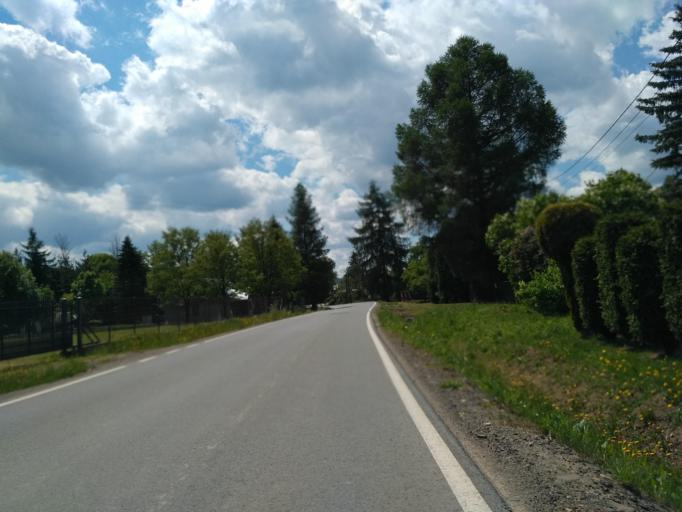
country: PL
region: Subcarpathian Voivodeship
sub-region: Powiat krosnienski
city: Dukla
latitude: 49.5775
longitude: 21.6963
